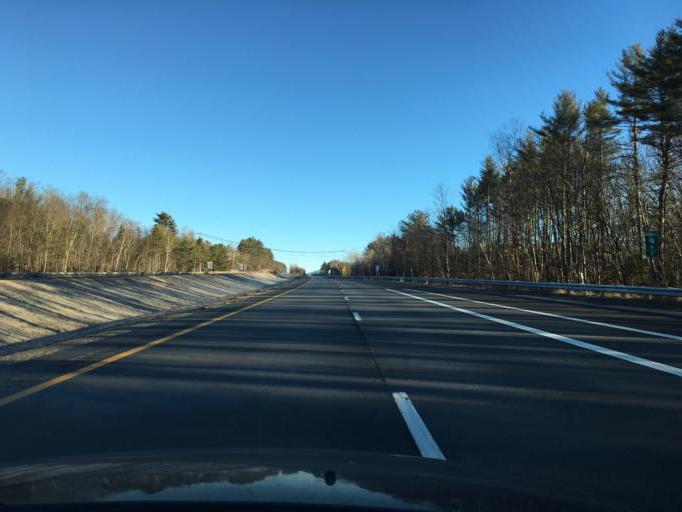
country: US
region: New Hampshire
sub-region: Grafton County
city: Plymouth
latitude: 43.7767
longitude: -71.6800
